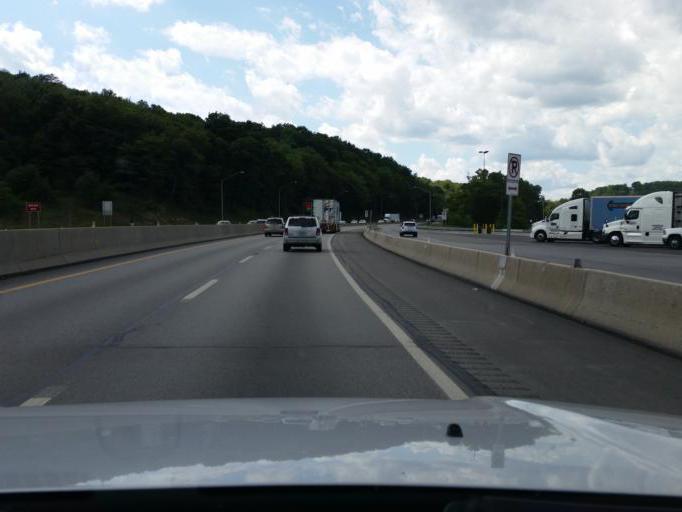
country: US
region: Pennsylvania
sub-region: Bedford County
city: Bedford
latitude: 40.0308
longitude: -78.4933
